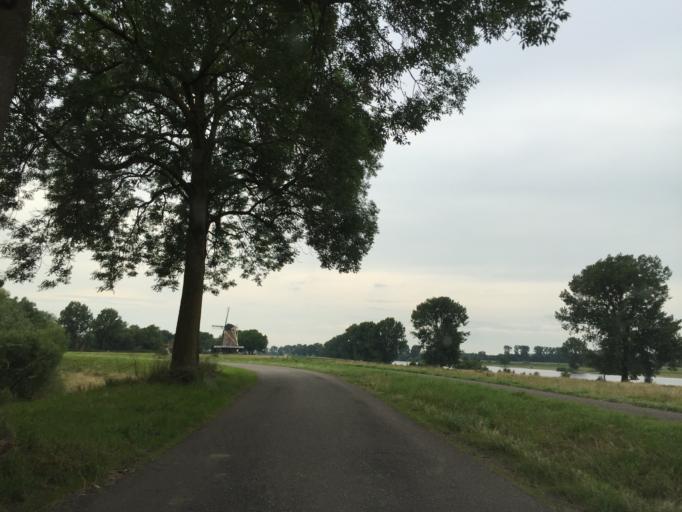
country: NL
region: Gelderland
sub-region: Gemeente Wijchen
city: Bergharen
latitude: 51.8179
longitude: 5.6190
